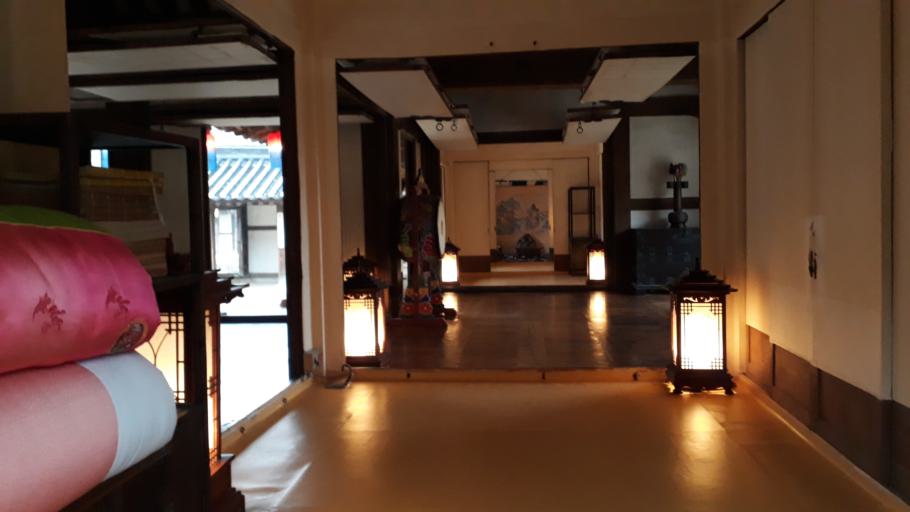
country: KR
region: Seoul
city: Seoul
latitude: 37.5617
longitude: 126.9919
